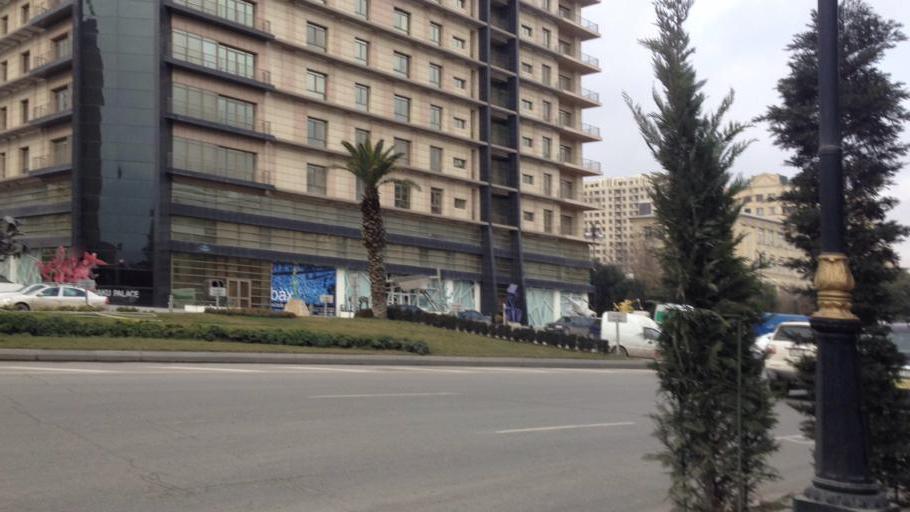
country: AZ
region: Baki
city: Baku
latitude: 40.3779
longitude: 49.8657
